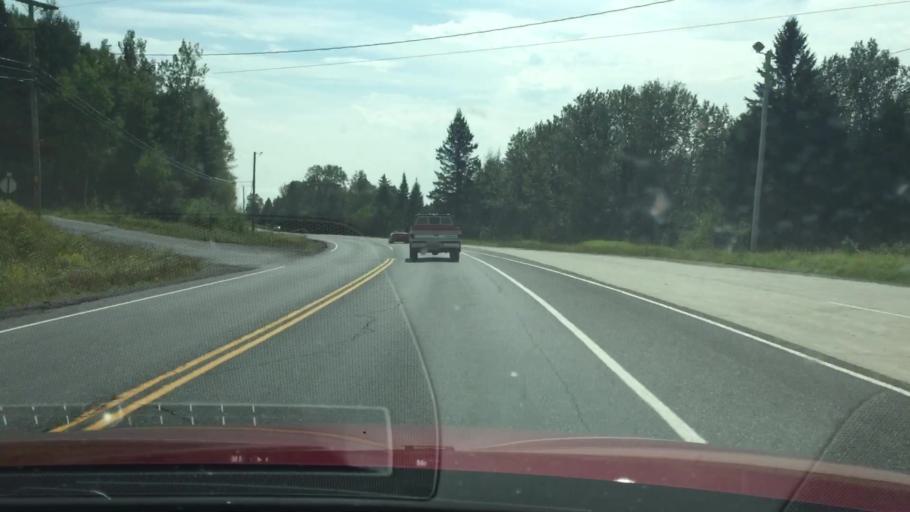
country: US
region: Maine
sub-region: Aroostook County
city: Presque Isle
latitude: 46.6219
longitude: -67.9891
